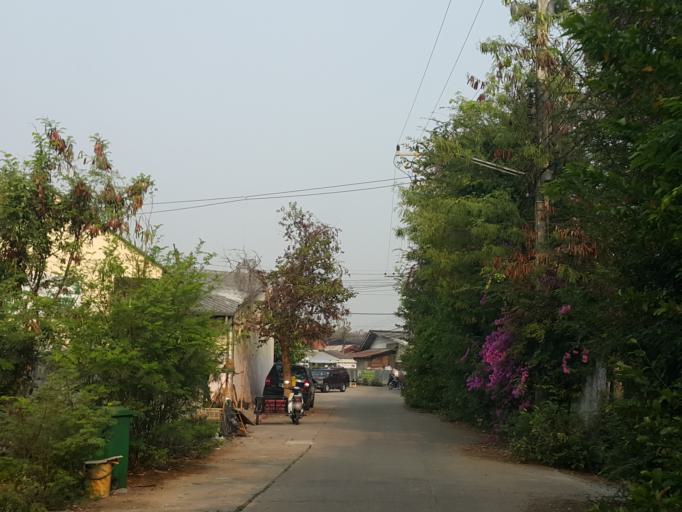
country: TH
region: Chiang Mai
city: San Kamphaeng
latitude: 18.7672
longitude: 99.0852
